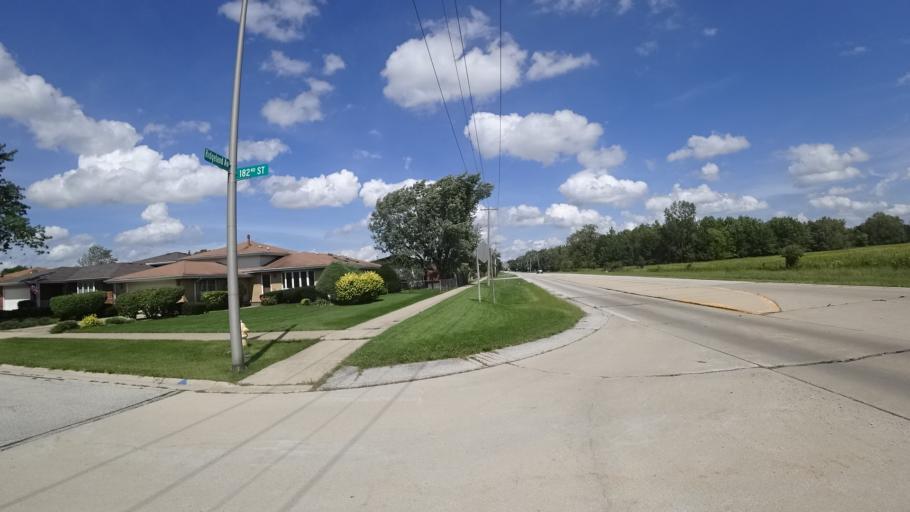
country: US
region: Illinois
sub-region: Cook County
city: Tinley Park
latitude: 41.5608
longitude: -87.7743
